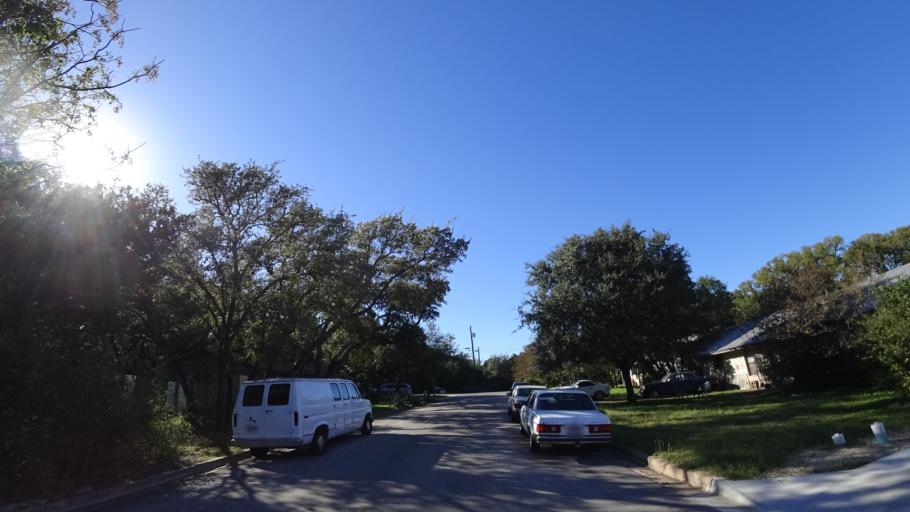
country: US
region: Texas
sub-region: Travis County
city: Rollingwood
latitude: 30.2382
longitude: -97.8076
